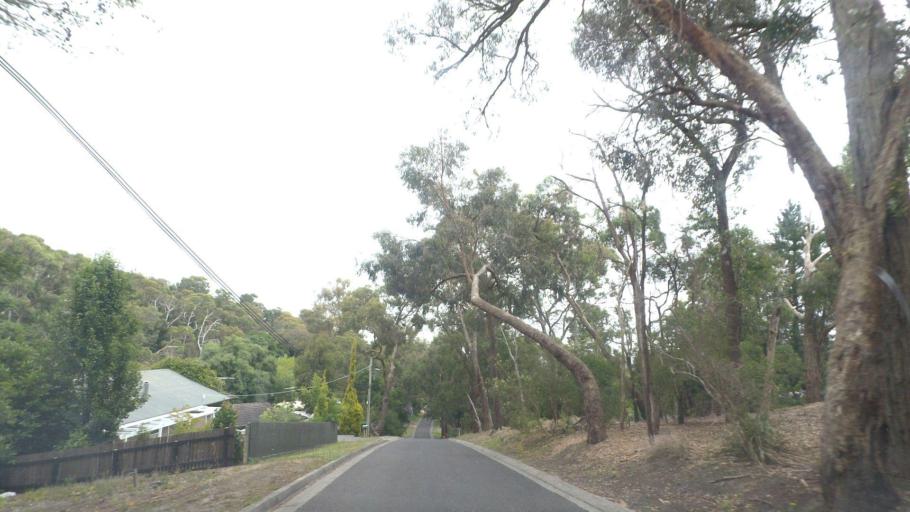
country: AU
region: Victoria
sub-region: Knox
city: The Basin
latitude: -37.8607
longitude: 145.3144
